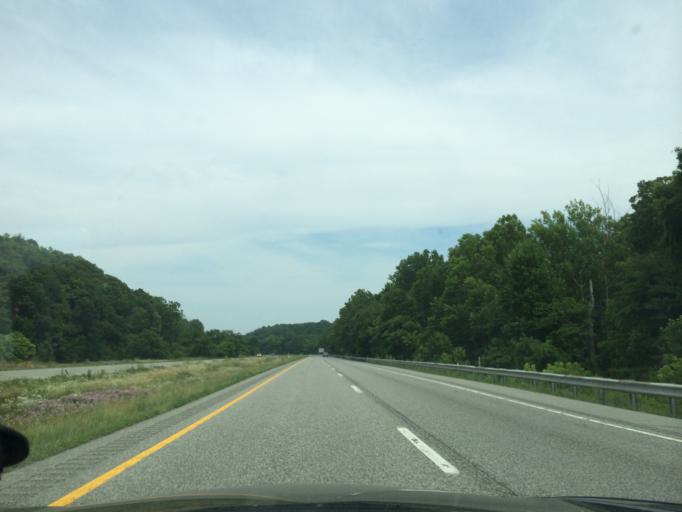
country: US
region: Maryland
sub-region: Washington County
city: Hancock
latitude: 39.7114
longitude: -78.2211
